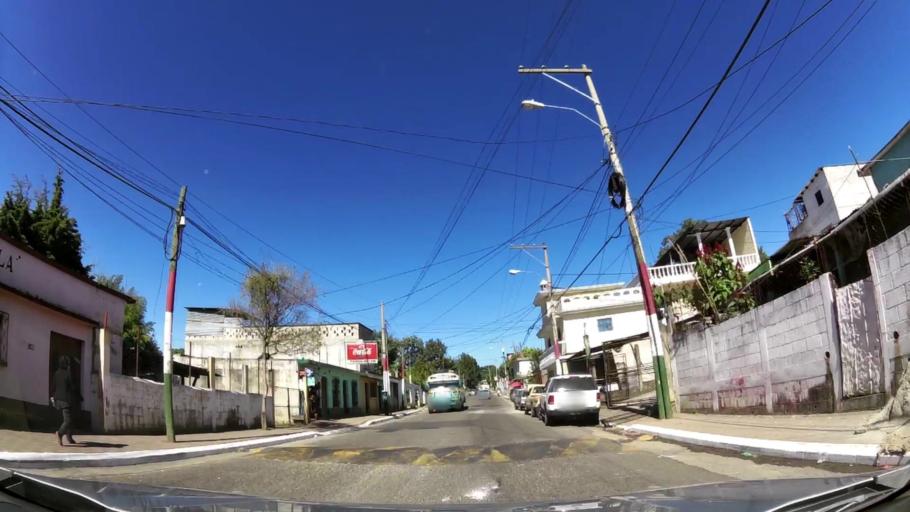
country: GT
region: Guatemala
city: Fraijanes
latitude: 14.4714
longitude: -90.4470
